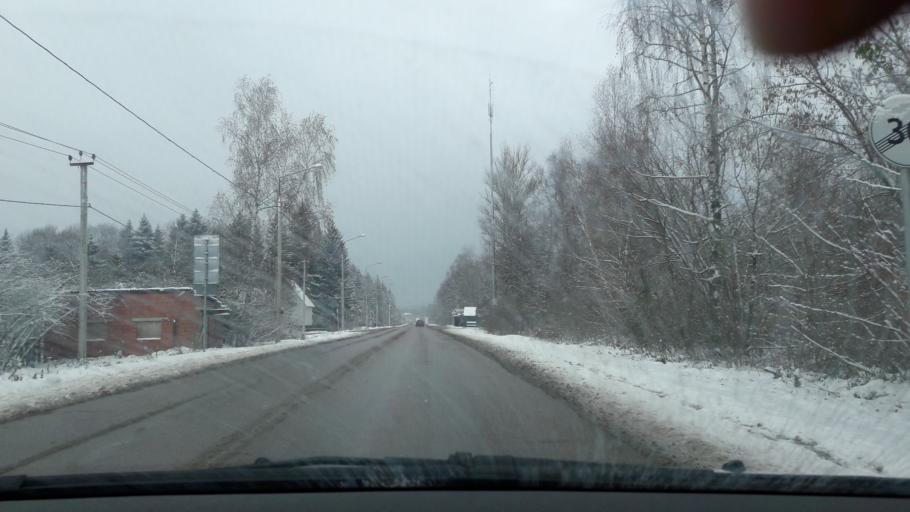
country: RU
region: Moskovskaya
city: Zvenigorod
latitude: 55.6266
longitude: 36.8655
